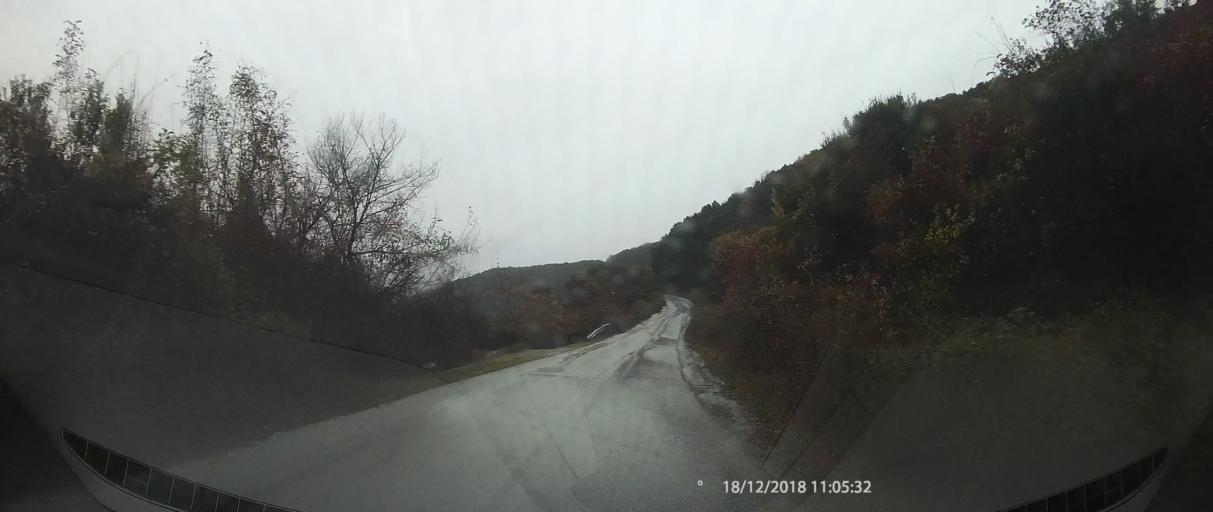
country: GR
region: Central Macedonia
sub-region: Nomos Pierias
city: Kato Milia
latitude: 40.2137
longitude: 22.3197
